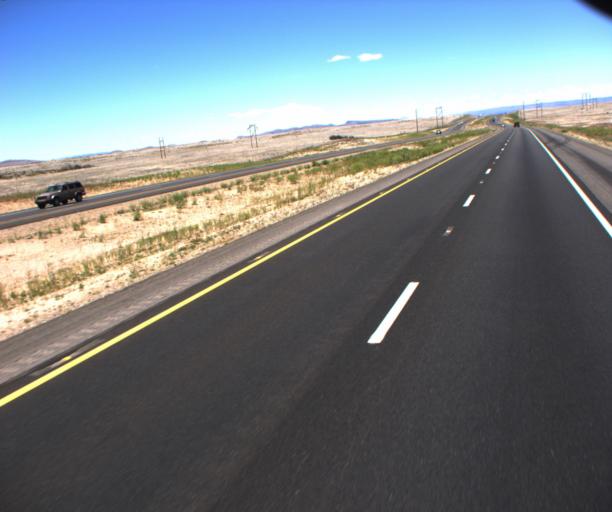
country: US
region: Arizona
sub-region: Yavapai County
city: Chino Valley
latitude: 34.6725
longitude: -112.4404
